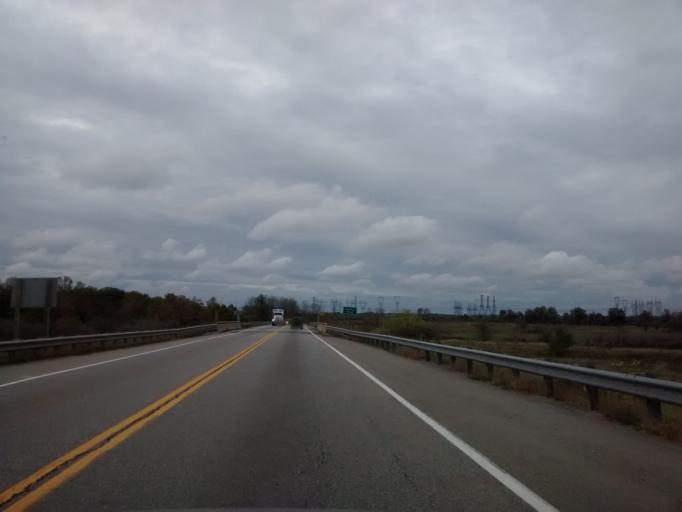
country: CA
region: Ontario
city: Ancaster
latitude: 43.0894
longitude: -79.9592
